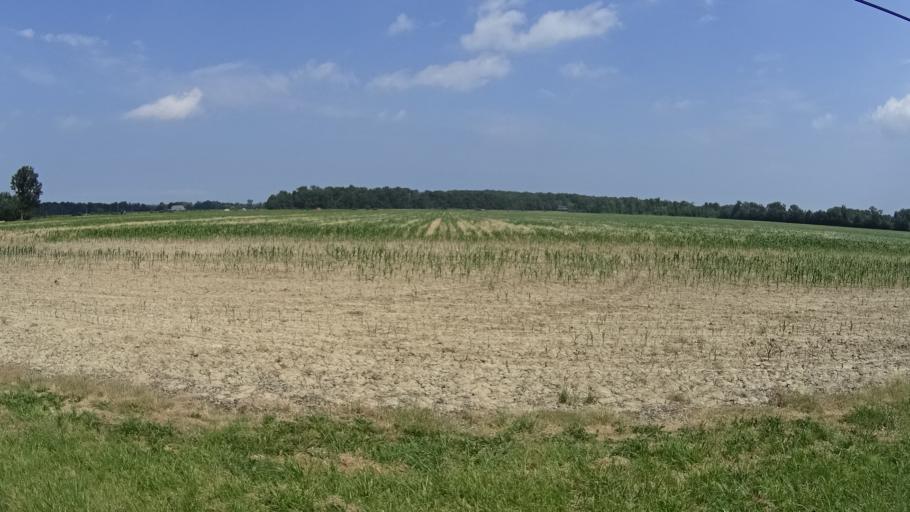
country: US
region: Ohio
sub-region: Lorain County
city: Vermilion
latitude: 41.3866
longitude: -82.3992
